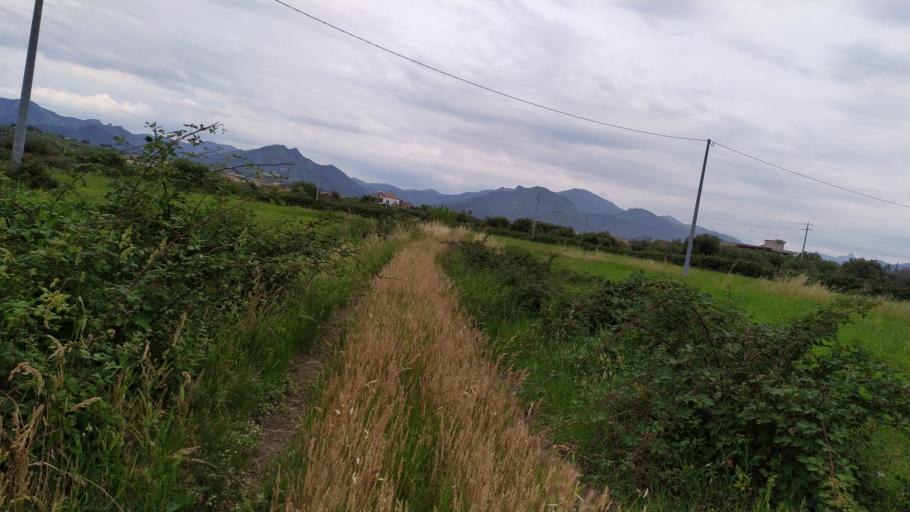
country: IT
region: Sicily
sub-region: Messina
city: San Filippo del Mela
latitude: 38.1852
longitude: 15.2616
